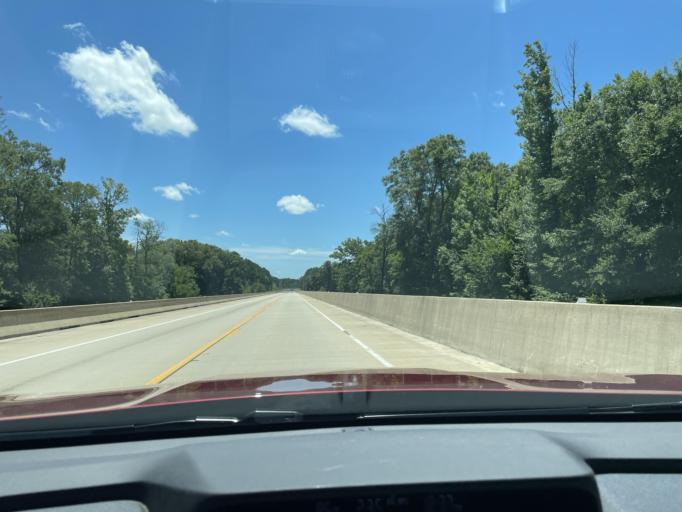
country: US
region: Arkansas
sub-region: Jefferson County
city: Pine Bluff
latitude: 34.1420
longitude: -91.9754
